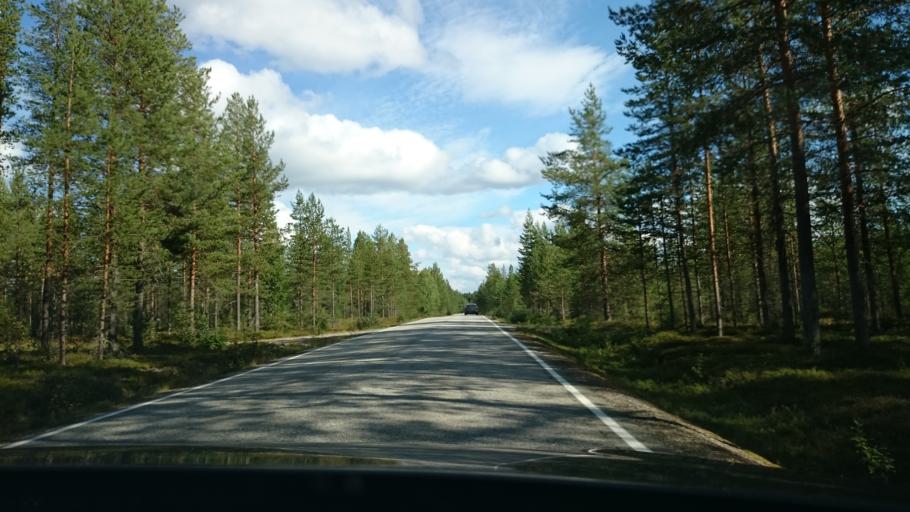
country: FI
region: Kainuu
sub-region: Kehys-Kainuu
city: Suomussalmi
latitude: 64.7509
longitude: 29.4246
